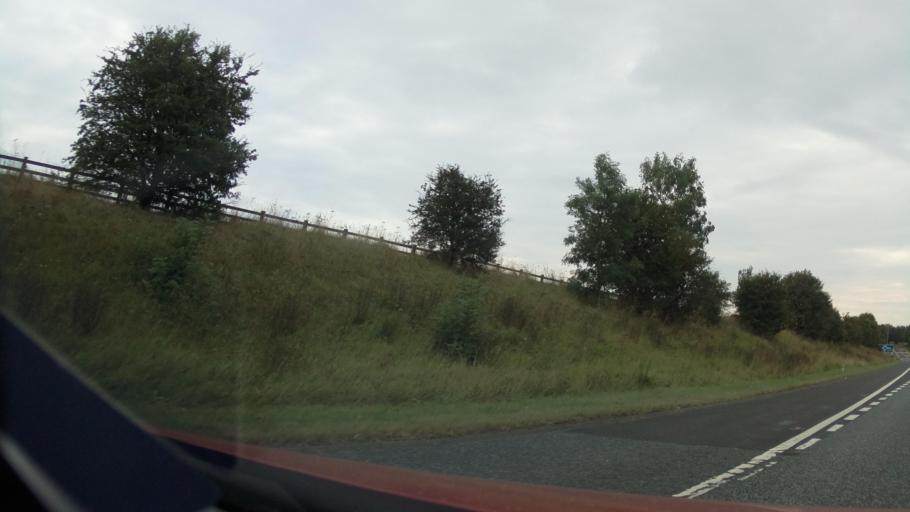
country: GB
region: England
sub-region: Darlington
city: Coatham Mundeville
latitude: 54.5600
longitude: -1.5905
